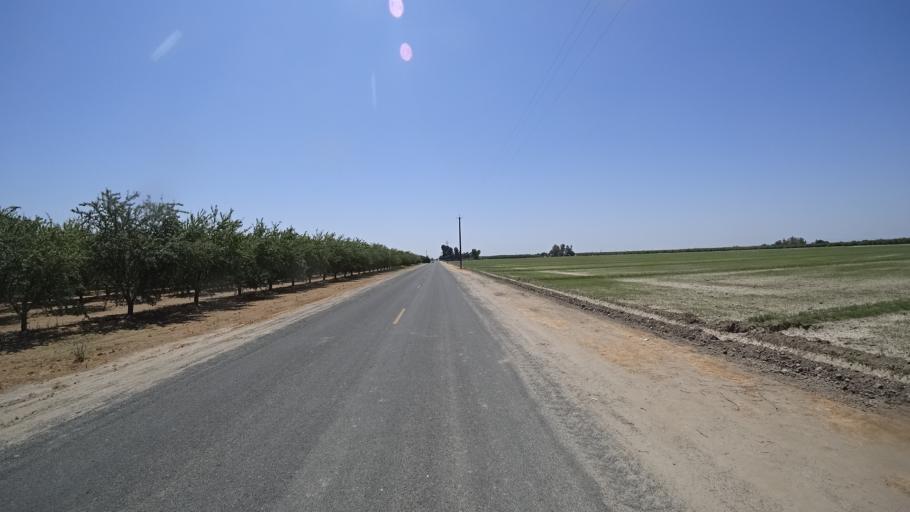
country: US
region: California
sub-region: Kings County
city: Armona
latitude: 36.2753
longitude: -119.7270
